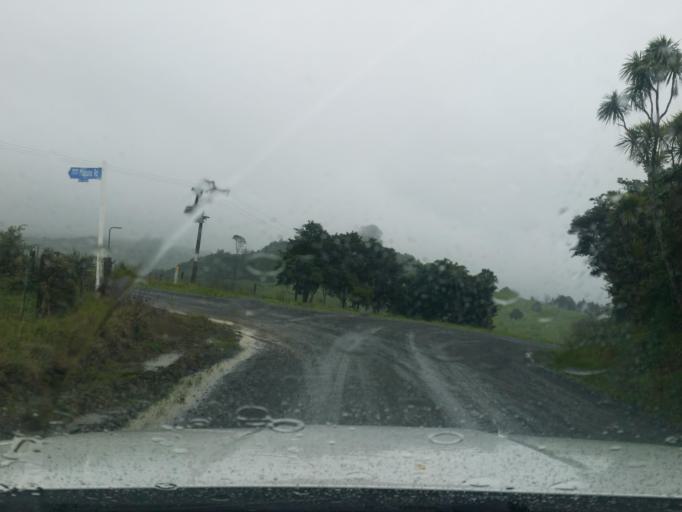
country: NZ
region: Northland
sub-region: Kaipara District
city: Dargaville
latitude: -35.8774
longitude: 174.0005
